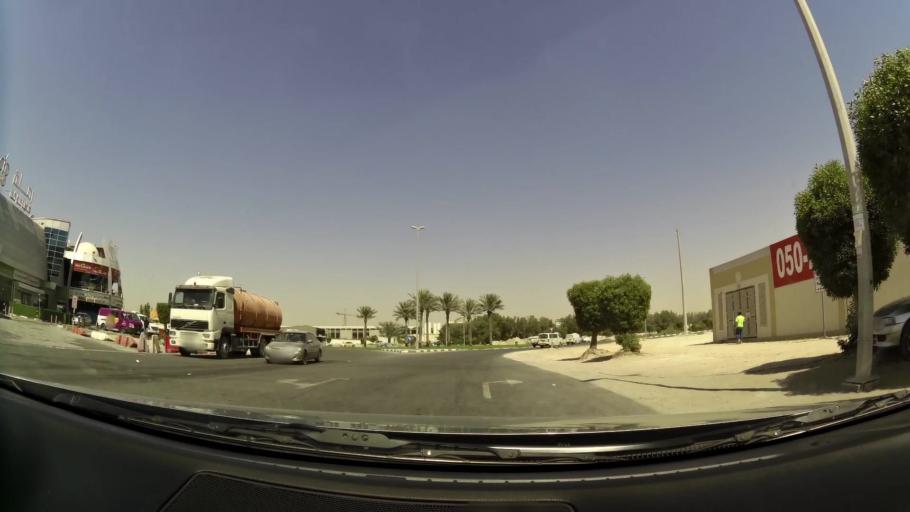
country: AE
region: Dubai
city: Dubai
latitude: 24.9703
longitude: 55.1715
